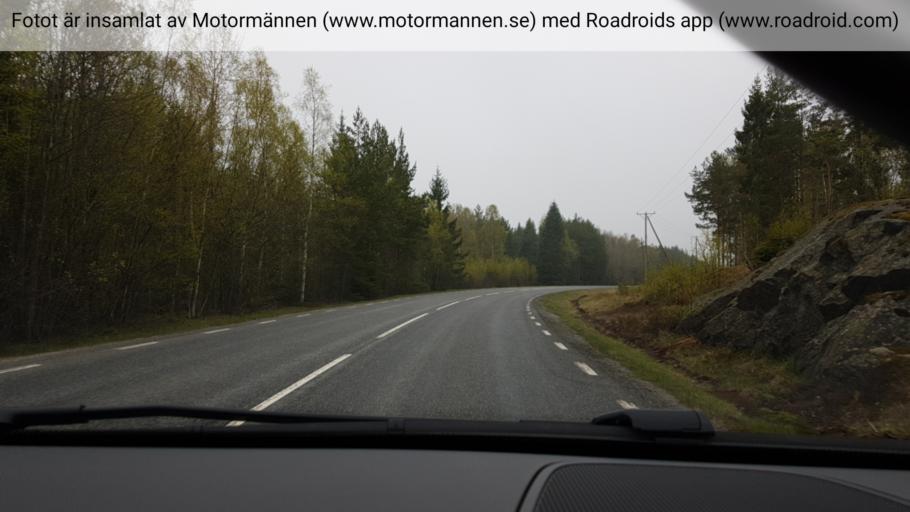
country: SE
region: Stockholm
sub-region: Nynashamns Kommun
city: Nynashamn
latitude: 58.9607
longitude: 17.9967
